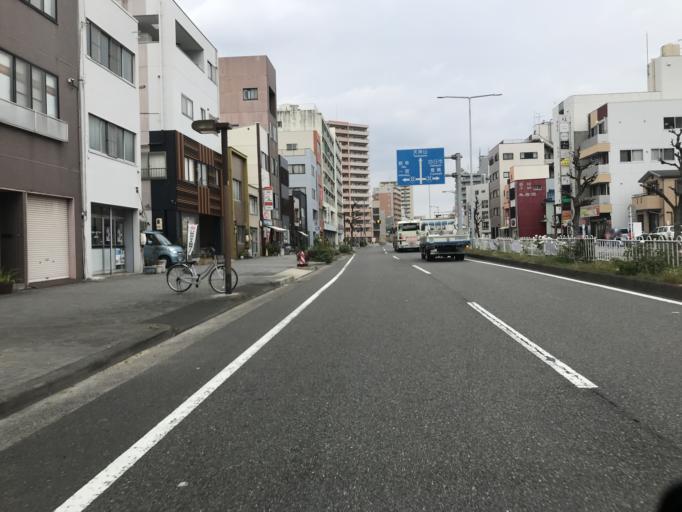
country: JP
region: Aichi
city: Nagoya-shi
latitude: 35.1834
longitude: 136.8860
